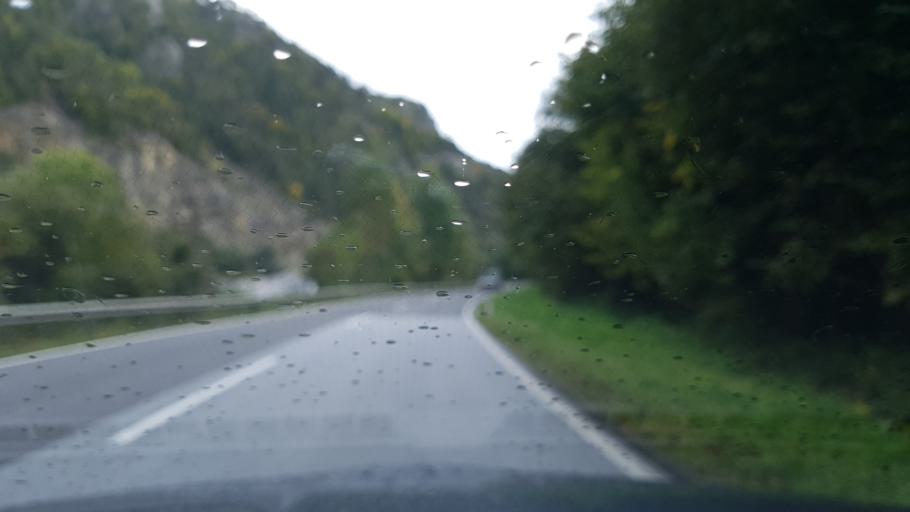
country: AT
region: Styria
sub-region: Politischer Bezirk Voitsberg
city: Piberegg
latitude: 47.0930
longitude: 15.0634
